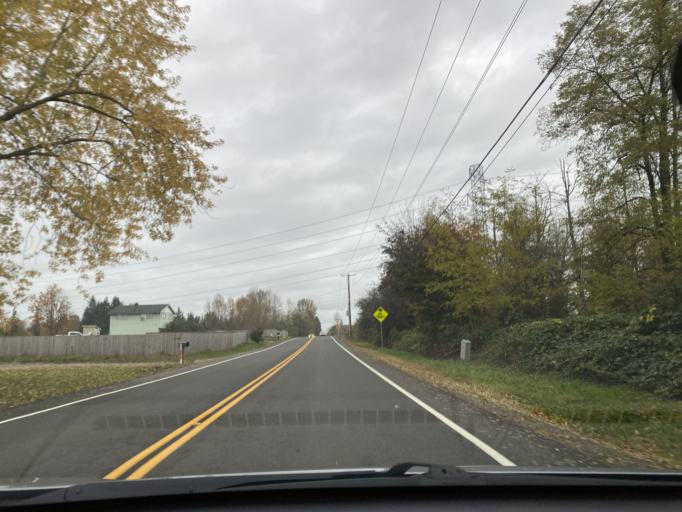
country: US
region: Washington
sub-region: King County
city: Lea Hill
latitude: 47.3007
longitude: -122.1495
